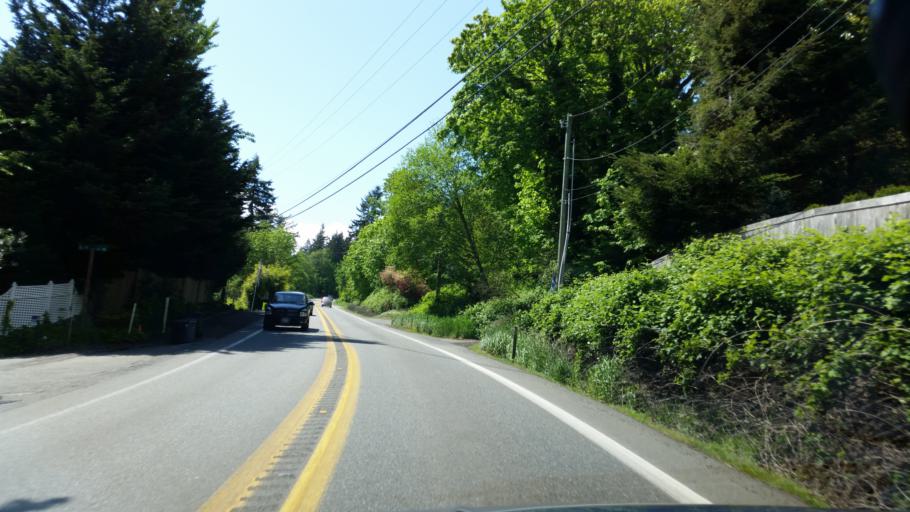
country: US
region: Washington
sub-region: Pierce County
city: Wauna
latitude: 47.3788
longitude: -122.6480
